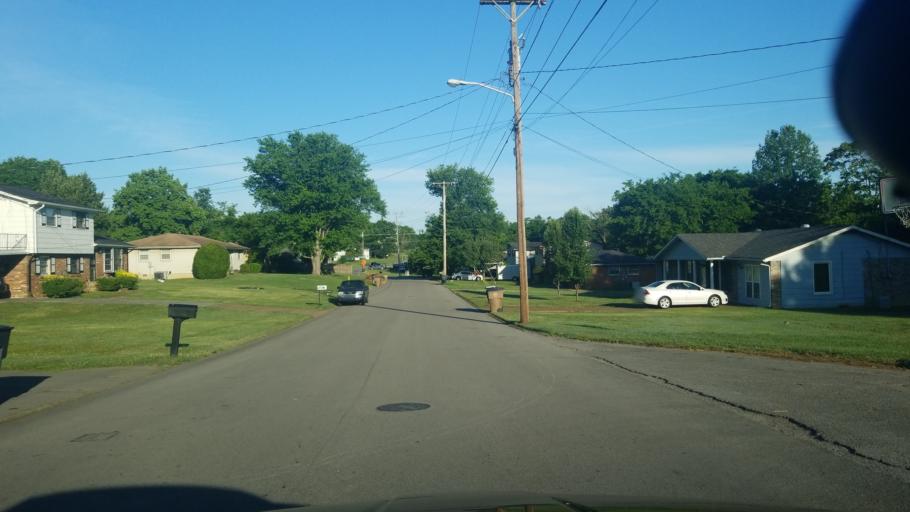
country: US
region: Tennessee
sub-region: Davidson County
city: Nashville
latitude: 36.2422
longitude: -86.7714
